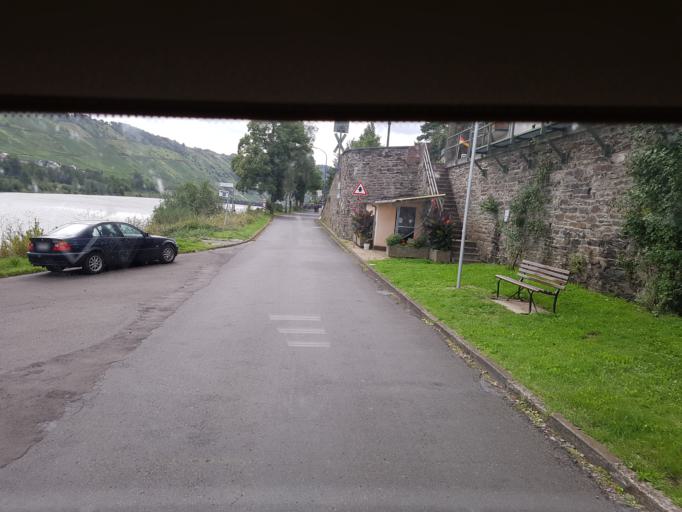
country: DE
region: Rheinland-Pfalz
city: Enkirch
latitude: 49.9831
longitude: 7.1185
